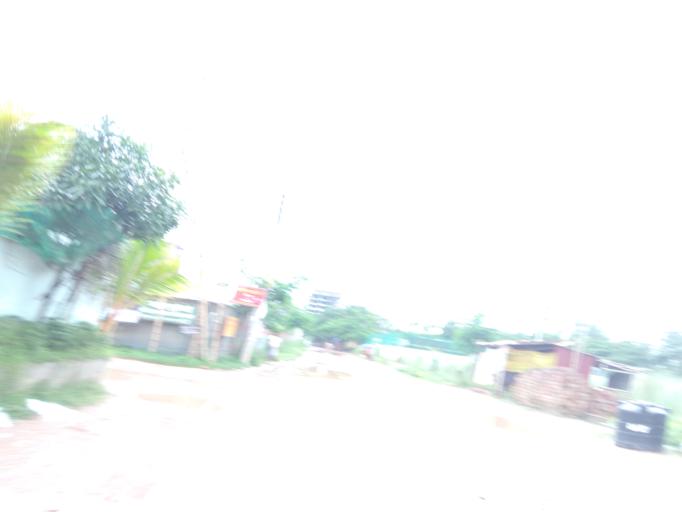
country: BD
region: Dhaka
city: Azimpur
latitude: 23.7530
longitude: 90.3507
